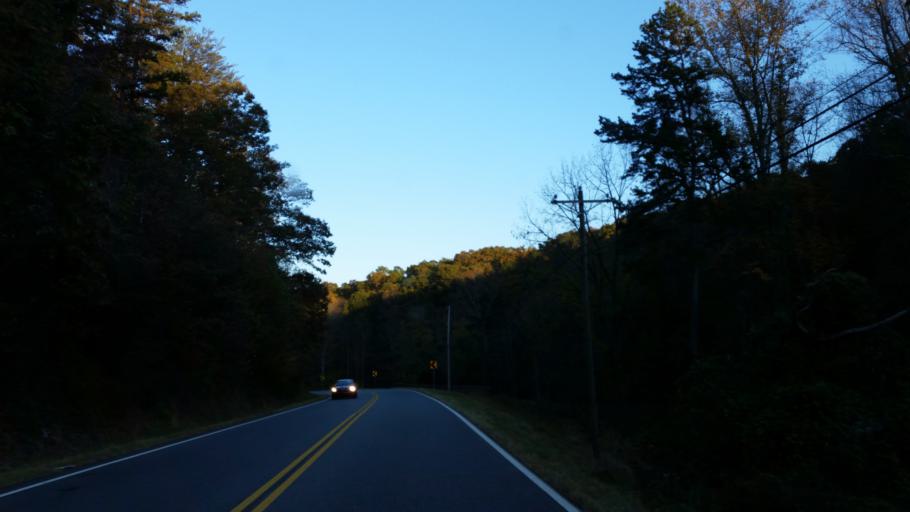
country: US
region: Georgia
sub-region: Lumpkin County
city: Dahlonega
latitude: 34.5285
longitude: -84.0191
